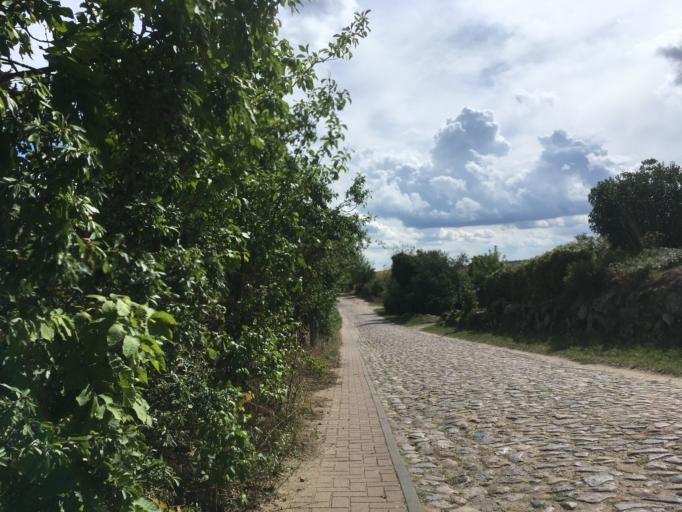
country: DE
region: Brandenburg
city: Gerswalde
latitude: 53.1294
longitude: 13.7996
